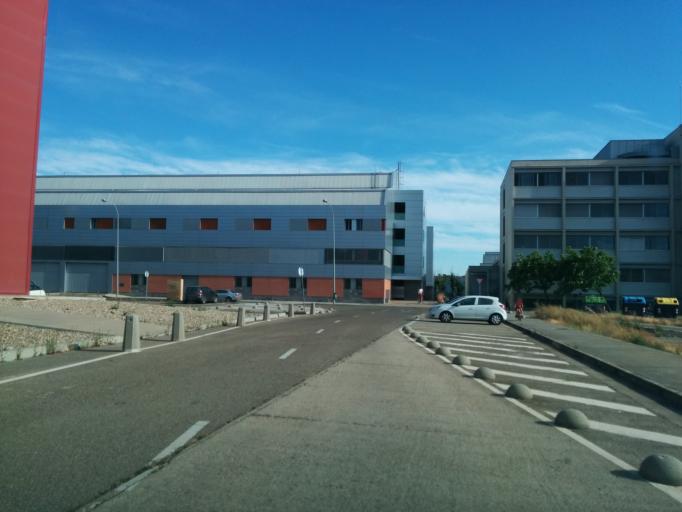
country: ES
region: Aragon
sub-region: Provincia de Zaragoza
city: Almozara
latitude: 41.6848
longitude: -0.8882
